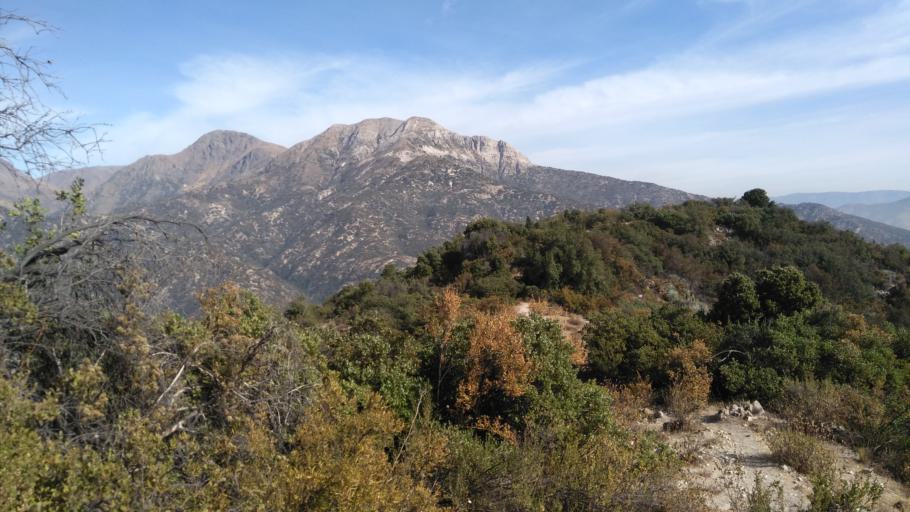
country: CL
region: Santiago Metropolitan
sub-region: Provincia de Cordillera
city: Puente Alto
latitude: -33.7200
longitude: -70.4528
